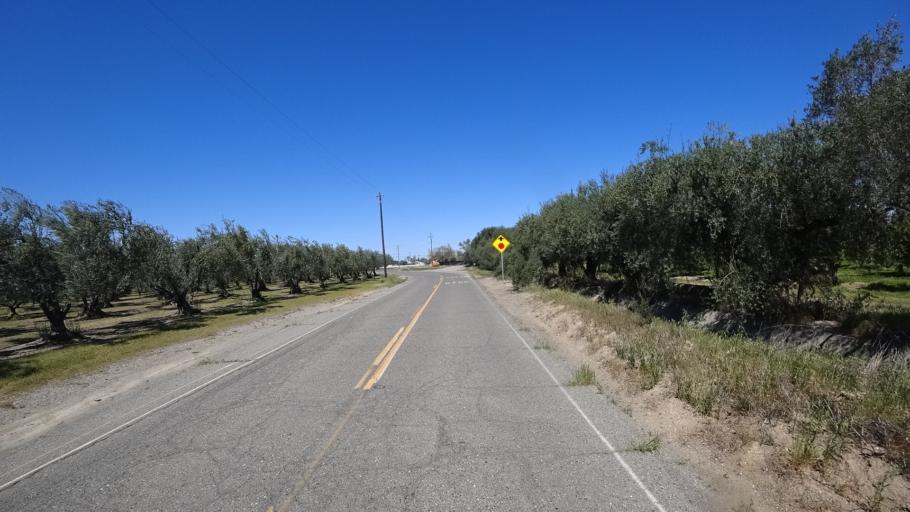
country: US
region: California
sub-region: Glenn County
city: Orland
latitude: 39.7453
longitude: -122.1594
